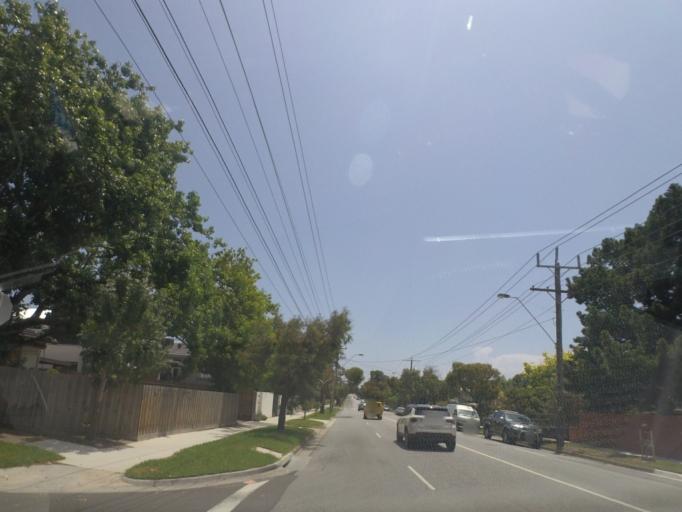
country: AU
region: Victoria
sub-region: Bayside
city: Hampton East
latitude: -37.9445
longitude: 145.0225
